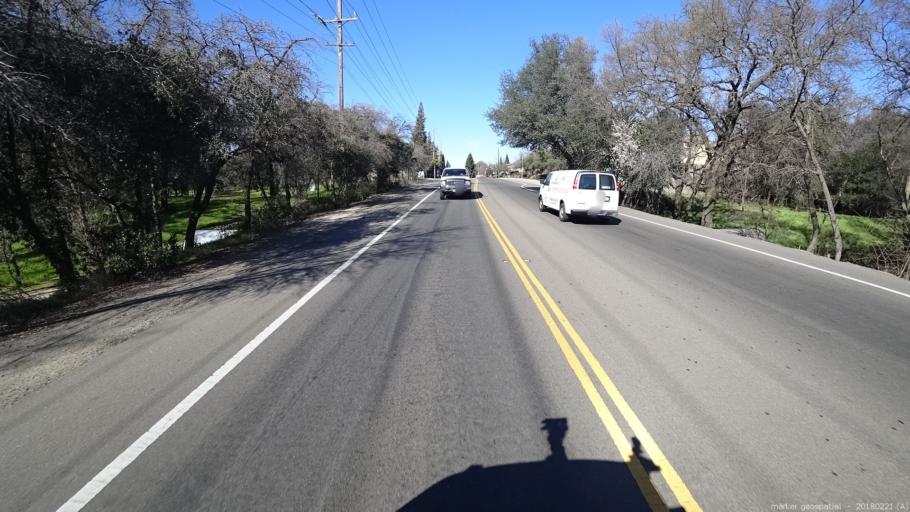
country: US
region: California
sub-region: Sacramento County
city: Citrus Heights
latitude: 38.6802
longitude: -121.2624
